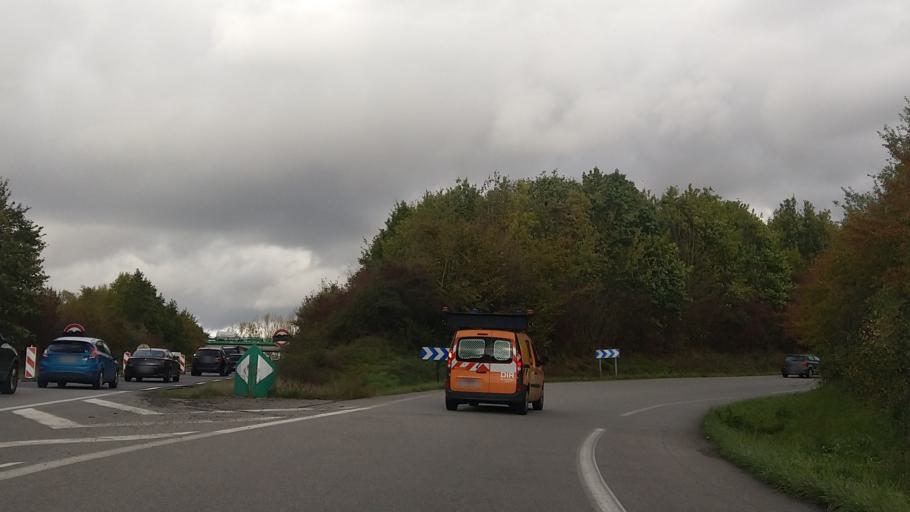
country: FR
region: Ile-de-France
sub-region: Departement du Val-d'Oise
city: Mours
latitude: 49.1264
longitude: 2.2544
